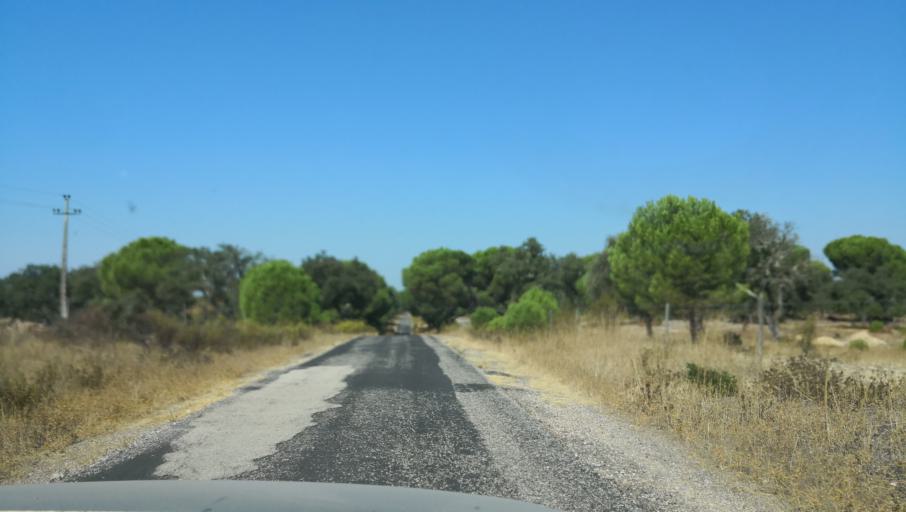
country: PT
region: Setubal
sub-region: Alcacer do Sal
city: Alcacer do Sal
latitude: 38.2626
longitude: -8.3111
